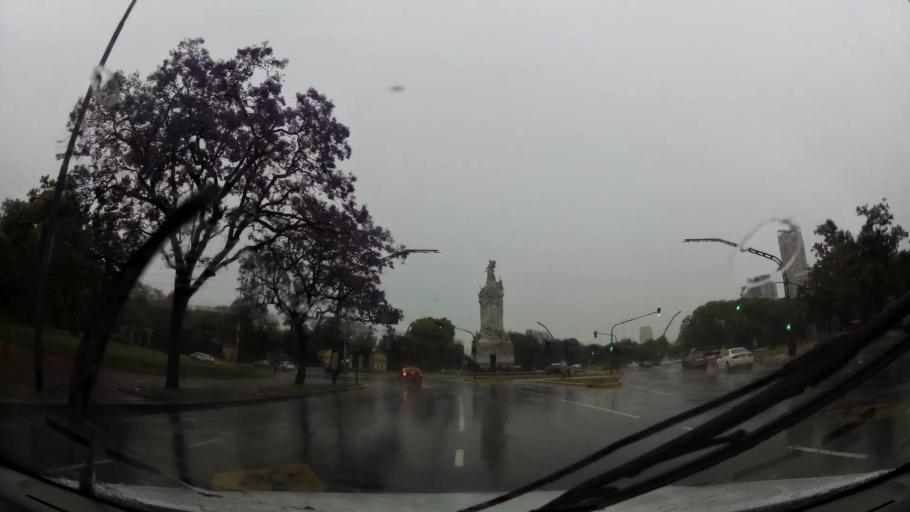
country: AR
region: Buenos Aires F.D.
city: Retiro
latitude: -34.5741
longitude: -58.4147
